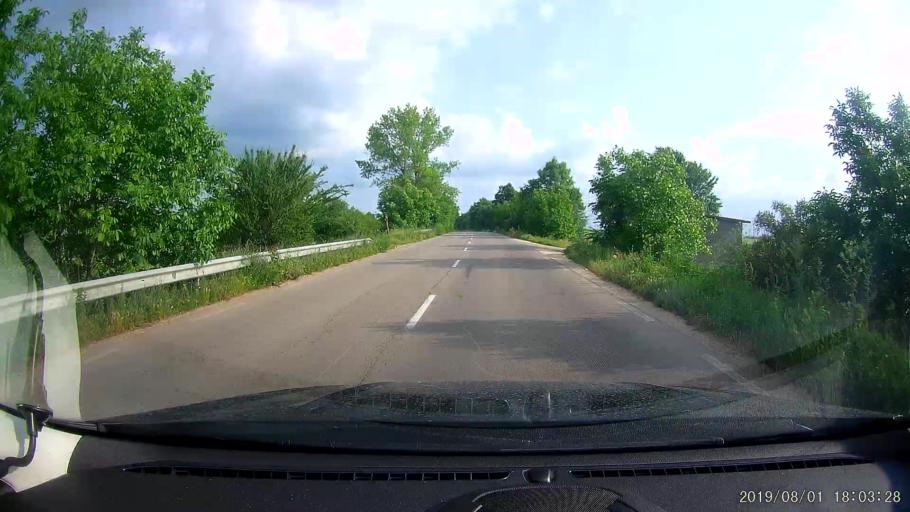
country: BG
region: Silistra
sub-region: Obshtina Alfatar
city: Alfatar
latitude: 43.9268
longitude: 27.2889
